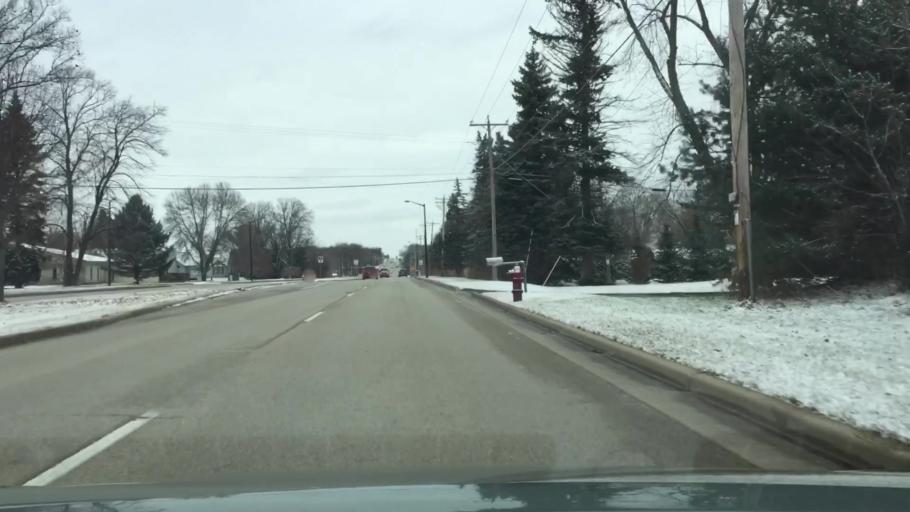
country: US
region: Wisconsin
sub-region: Waukesha County
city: Butler
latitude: 43.1152
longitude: -88.1053
